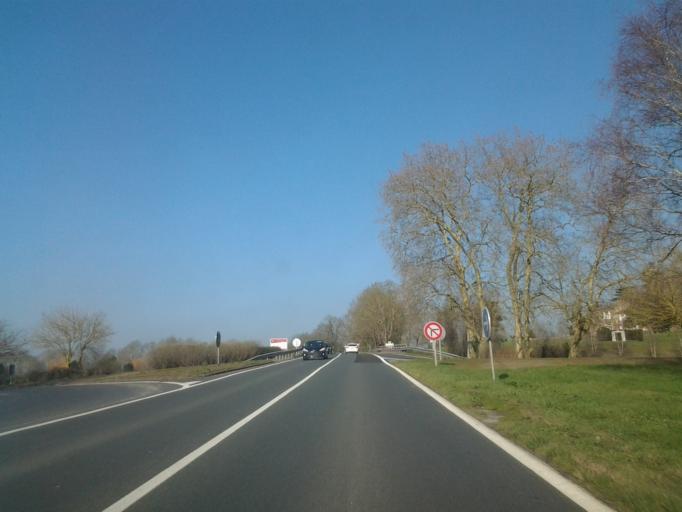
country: FR
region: Pays de la Loire
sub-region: Departement de la Vendee
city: Saint-Christophe-du-Ligneron
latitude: 46.8199
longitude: -1.7637
